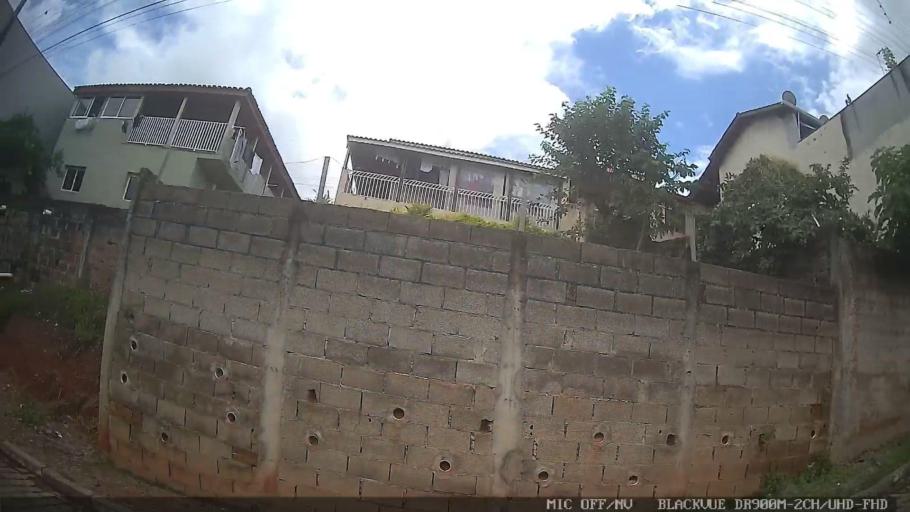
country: BR
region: Minas Gerais
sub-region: Extrema
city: Extrema
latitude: -22.7925
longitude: -46.4419
